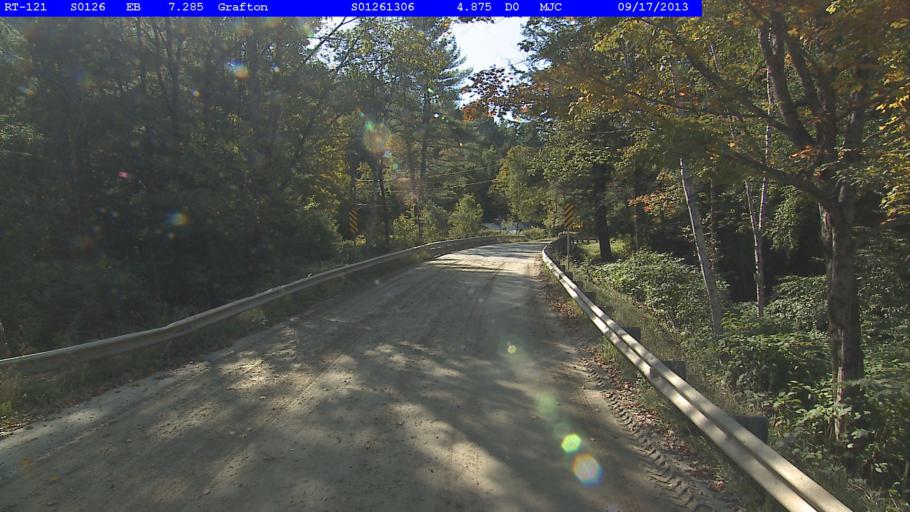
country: US
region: Vermont
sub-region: Windsor County
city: Chester
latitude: 43.1810
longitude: -72.6118
